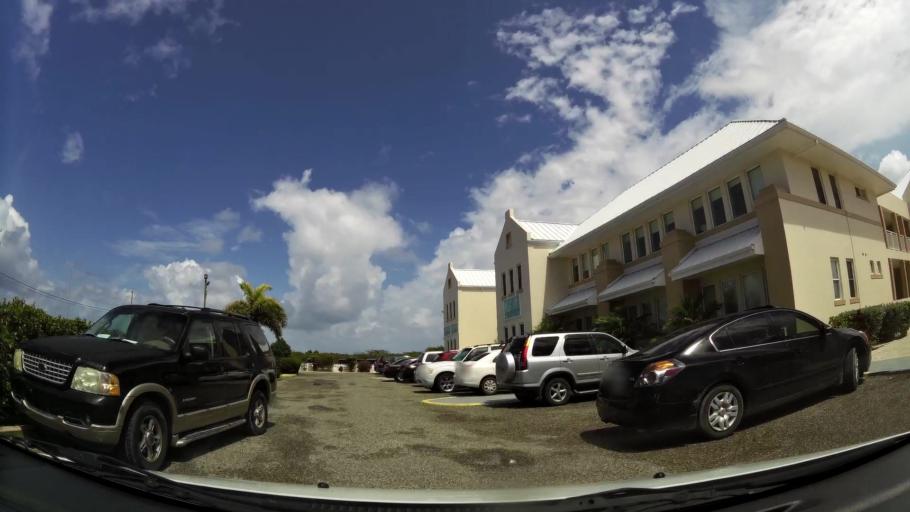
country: TC
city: Cockburn Town
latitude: 21.4419
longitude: -71.1483
